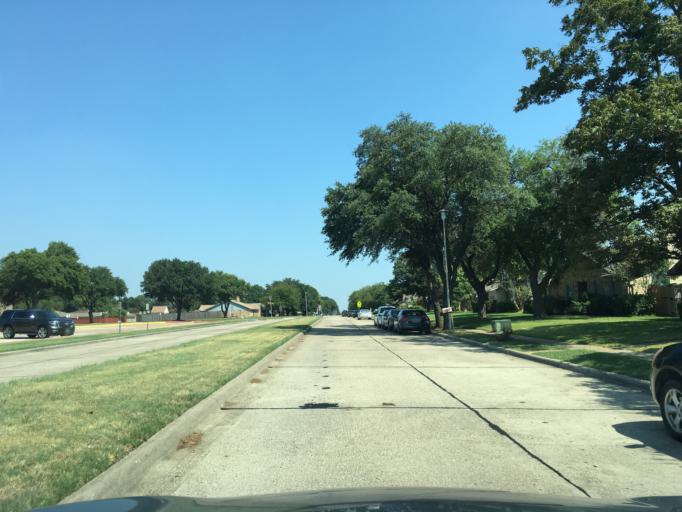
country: US
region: Texas
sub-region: Dallas County
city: Garland
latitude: 32.9347
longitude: -96.6572
